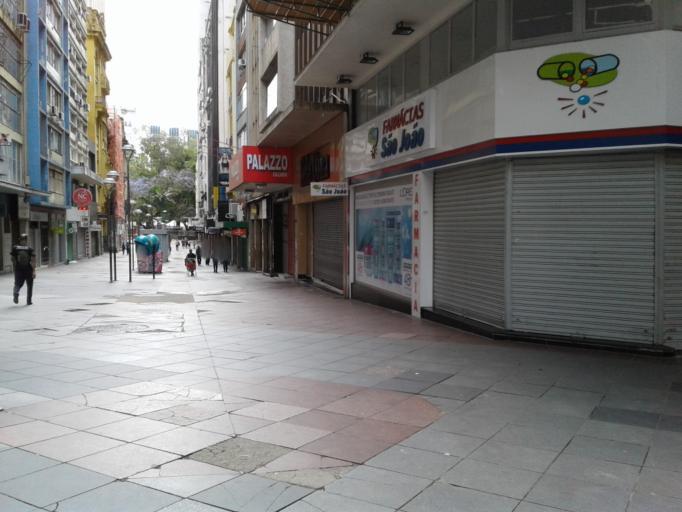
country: BR
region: Rio Grande do Sul
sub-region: Porto Alegre
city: Porto Alegre
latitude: -30.0298
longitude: -51.2286
